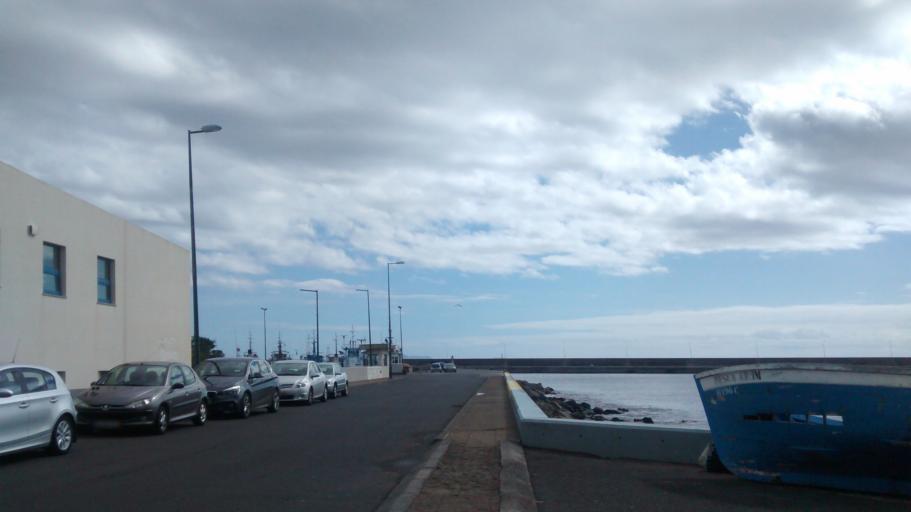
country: PT
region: Madeira
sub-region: Machico
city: Canical
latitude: 32.7369
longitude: -16.7364
